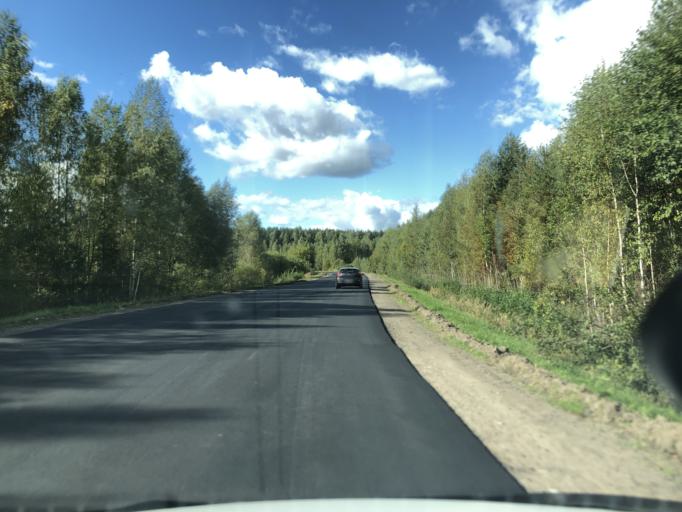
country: RU
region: Jaroslavl
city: Porech'ye-Rybnoye
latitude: 56.9721
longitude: 39.4117
